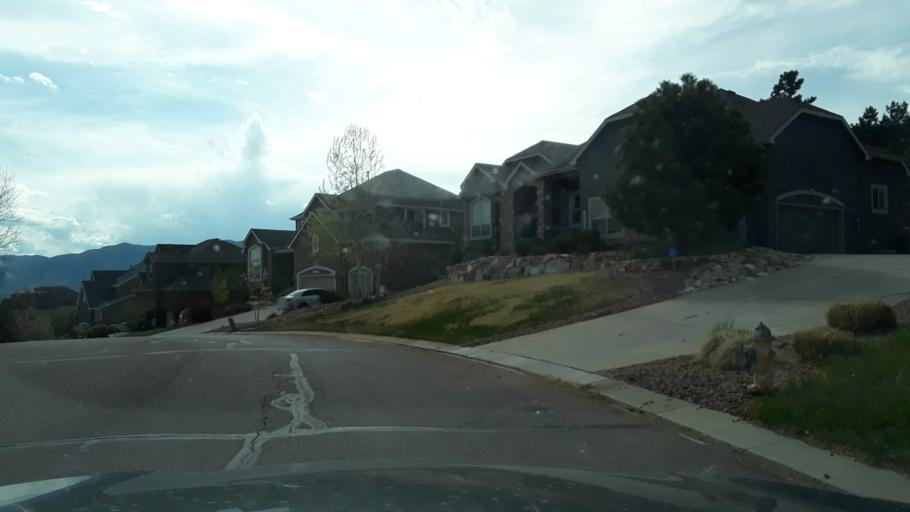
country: US
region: Colorado
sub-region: El Paso County
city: Gleneagle
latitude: 39.0146
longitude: -104.7956
